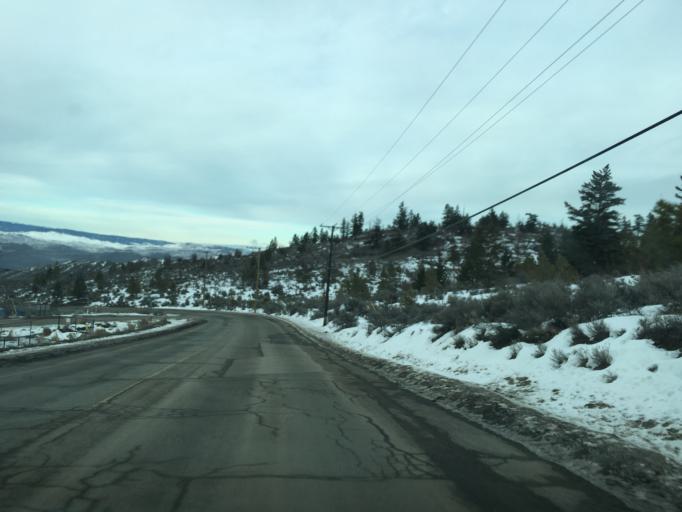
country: CA
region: British Columbia
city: Kamloops
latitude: 50.6585
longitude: -120.4355
